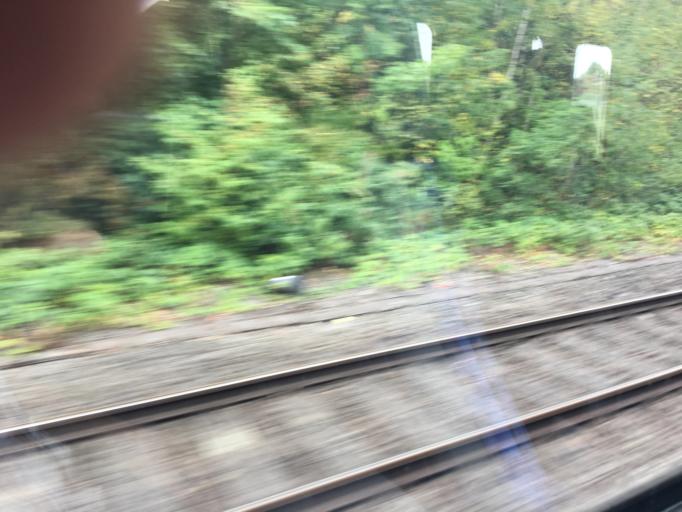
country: DE
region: North Rhine-Westphalia
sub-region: Regierungsbezirk Arnsberg
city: Dortmund
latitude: 51.5093
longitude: 7.4243
